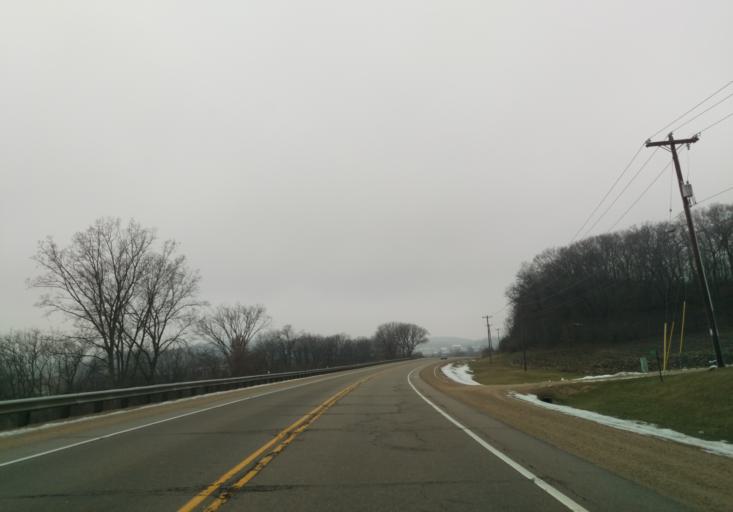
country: US
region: Wisconsin
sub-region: Dane County
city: Cross Plains
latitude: 43.0990
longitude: -89.6278
